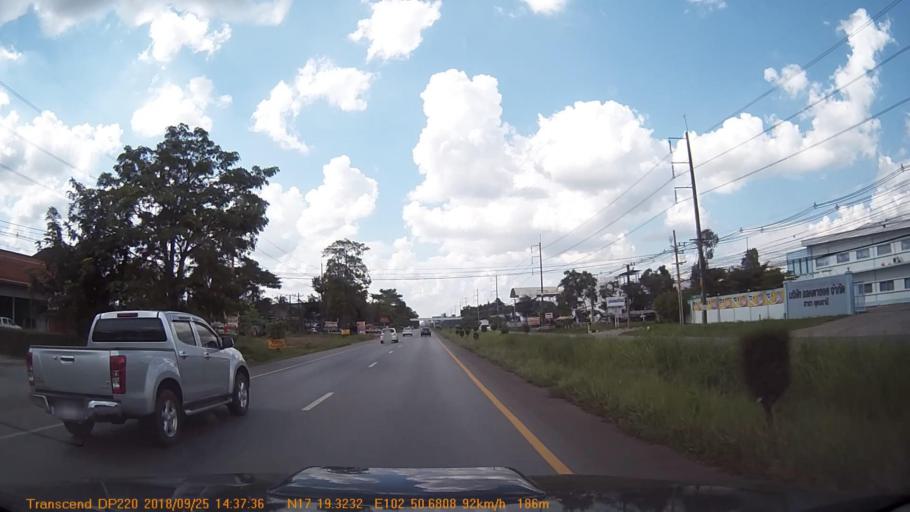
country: TH
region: Changwat Udon Thani
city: Udon Thani
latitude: 17.3223
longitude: 102.8445
